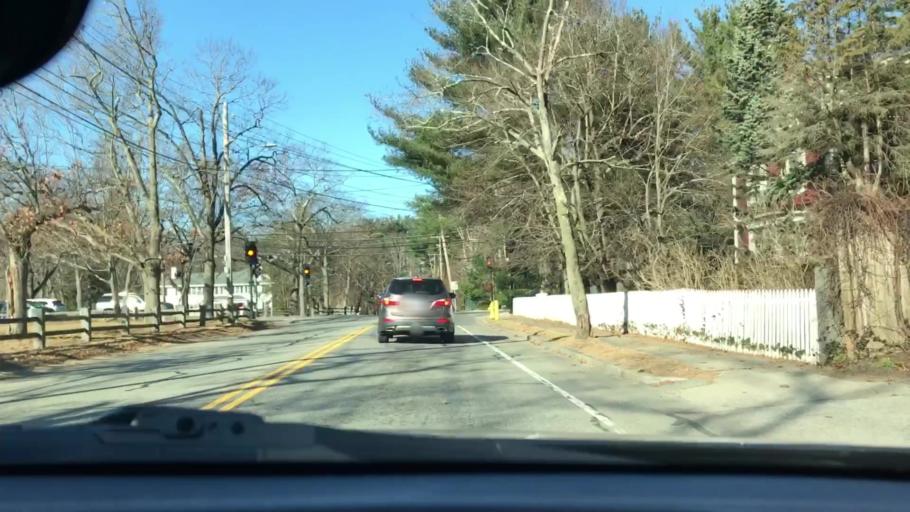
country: US
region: Massachusetts
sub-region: Norfolk County
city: Dedham
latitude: 42.2517
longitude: -71.1839
